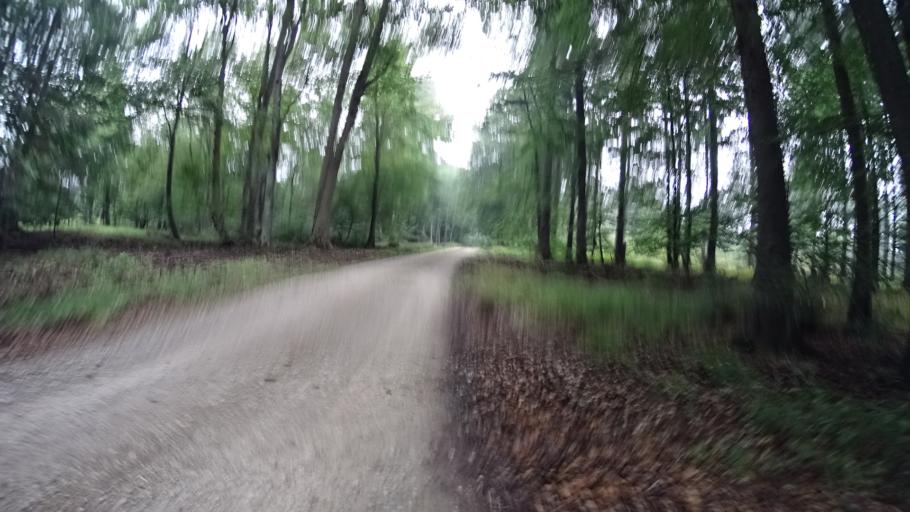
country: DE
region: Bavaria
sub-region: Upper Bavaria
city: Stammham
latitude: 48.8828
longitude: 11.5101
